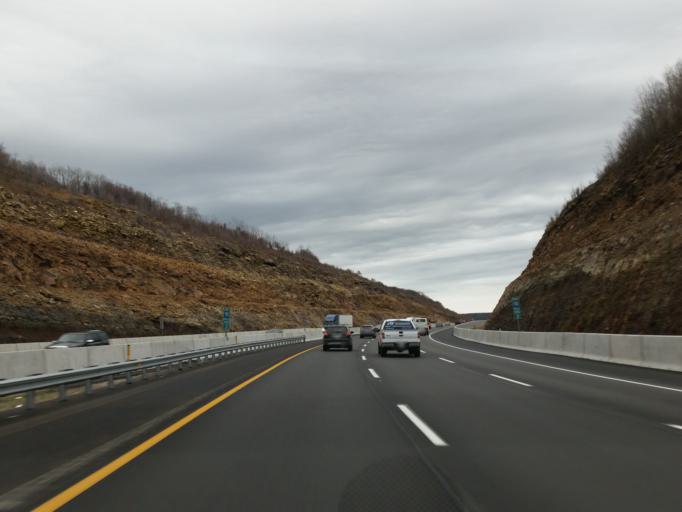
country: US
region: Pennsylvania
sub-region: Westmoreland County
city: Ligonier
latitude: 40.1078
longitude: -79.2214
